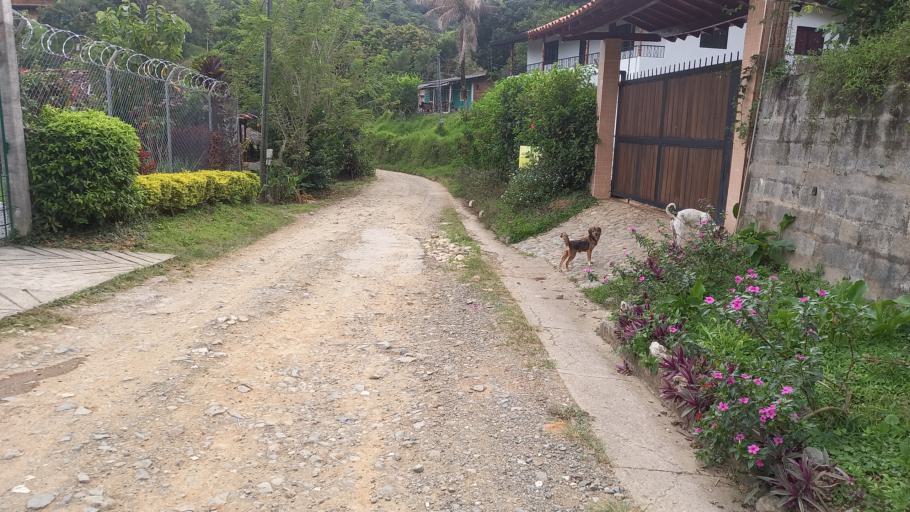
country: CO
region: Antioquia
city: Santa Barbara
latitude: 5.8383
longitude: -75.5741
